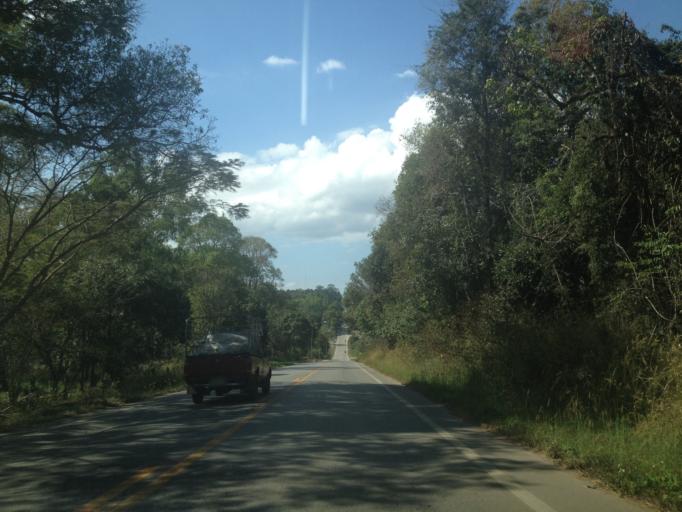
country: TH
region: Chiang Mai
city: Hot
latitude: 18.1455
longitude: 98.3610
